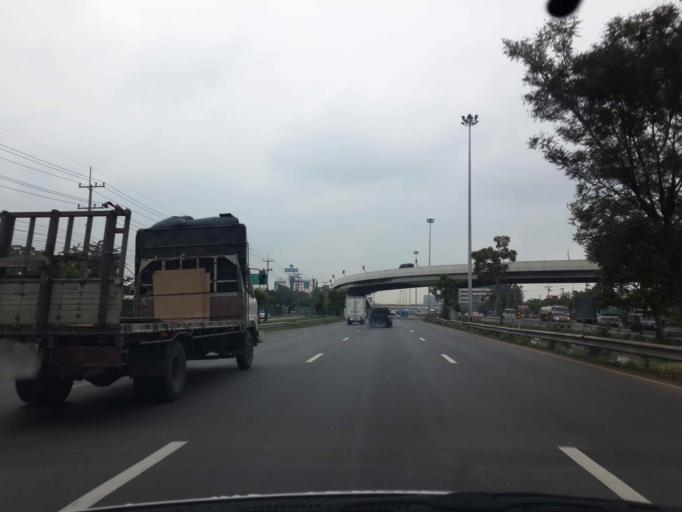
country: TH
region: Samut Sakhon
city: Samut Sakhon
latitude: 13.5615
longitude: 100.2756
